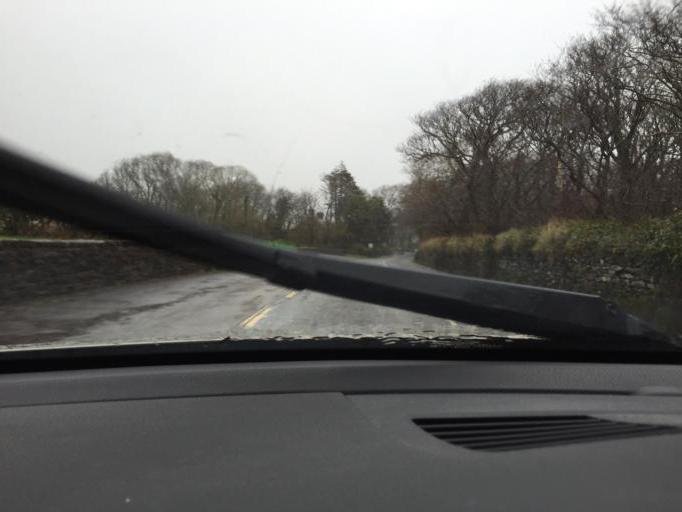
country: IE
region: Munster
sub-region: Ciarrai
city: Dingle
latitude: 52.1299
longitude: -10.3126
